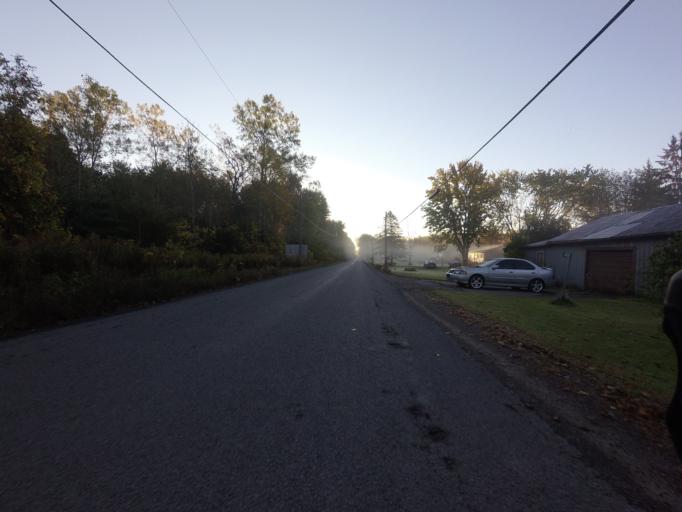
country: CA
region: Ontario
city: Quinte West
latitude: 44.0366
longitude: -77.5878
